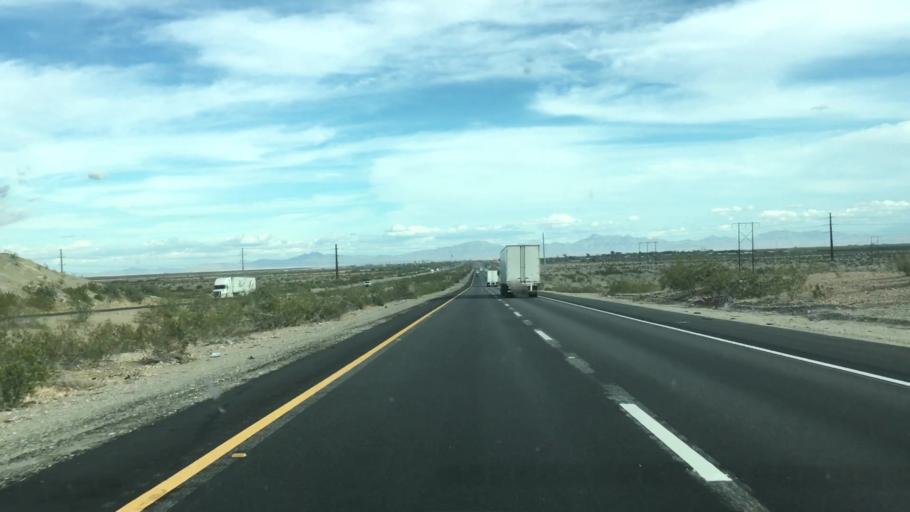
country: US
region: California
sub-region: Riverside County
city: Mesa Verde
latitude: 33.6087
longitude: -114.7607
